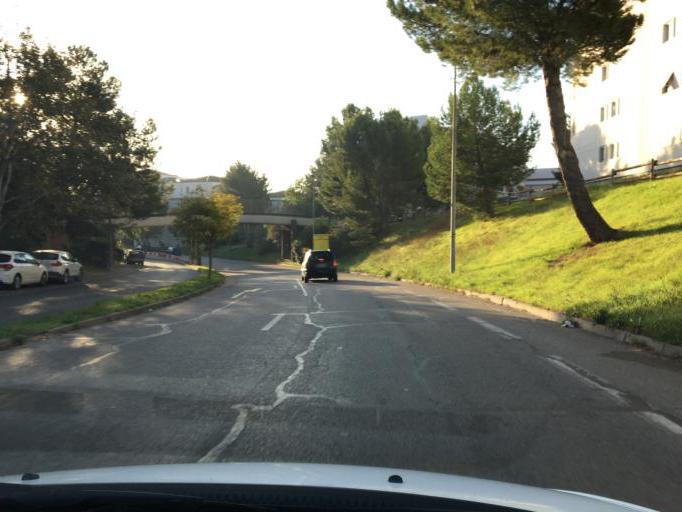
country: FR
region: Provence-Alpes-Cote d'Azur
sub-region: Departement des Bouches-du-Rhone
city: Aix-en-Provence
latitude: 43.5252
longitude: 5.4136
